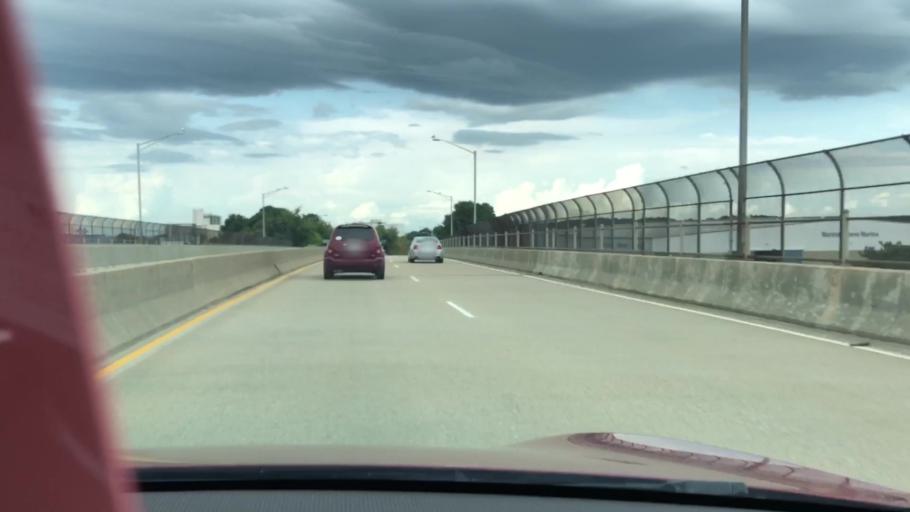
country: US
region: Virginia
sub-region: City of Virginia Beach
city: Virginia Beach
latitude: 36.9037
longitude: -76.0672
